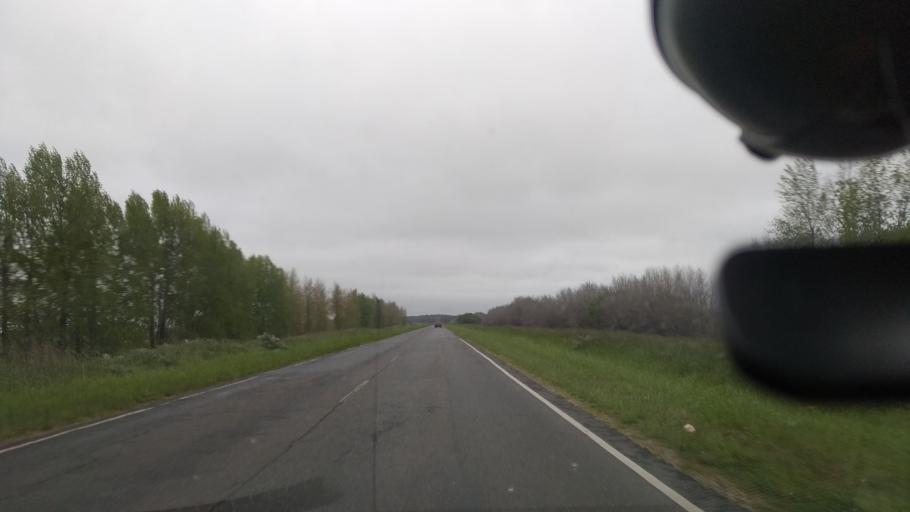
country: AR
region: Buenos Aires
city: Veronica
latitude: -35.4883
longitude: -57.3285
